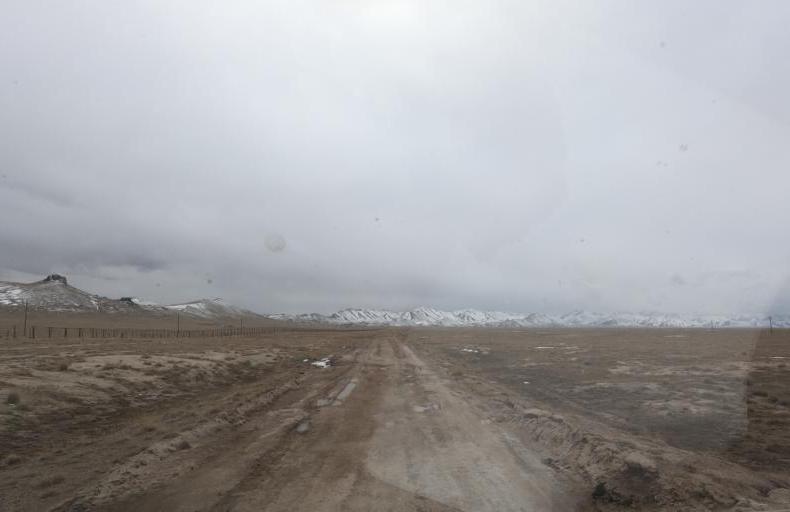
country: KG
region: Naryn
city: At-Bashi
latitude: 40.6417
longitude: 75.4297
